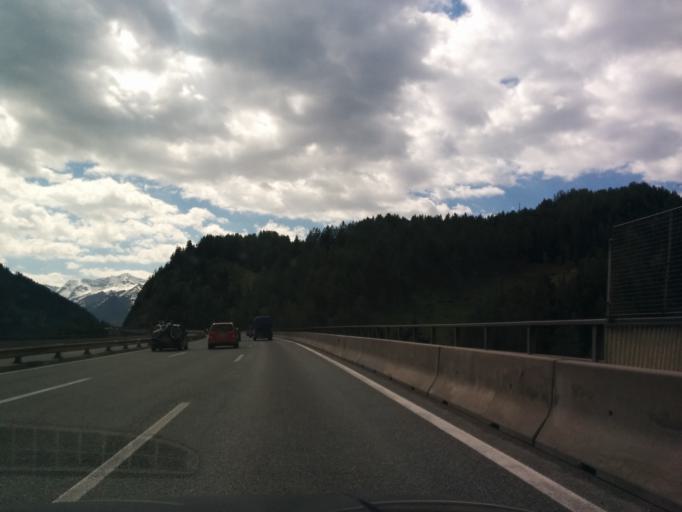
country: AT
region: Tyrol
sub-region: Politischer Bezirk Innsbruck Land
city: Steinach am Brenner
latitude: 47.0786
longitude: 11.4710
